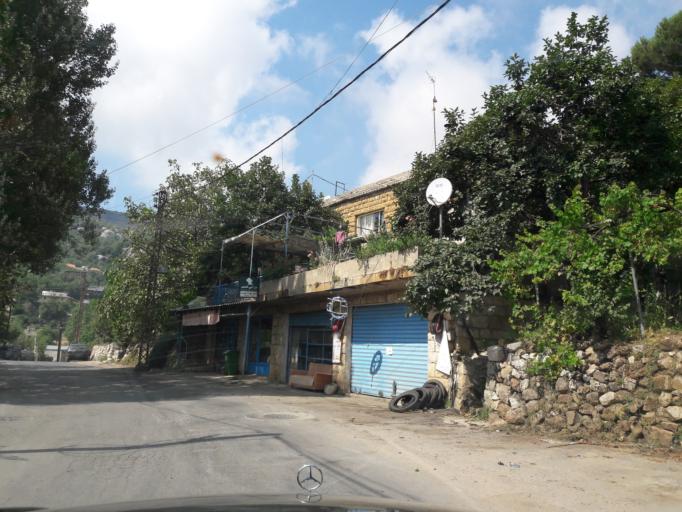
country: LB
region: Mont-Liban
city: Djounie
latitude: 33.9614
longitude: 35.7800
